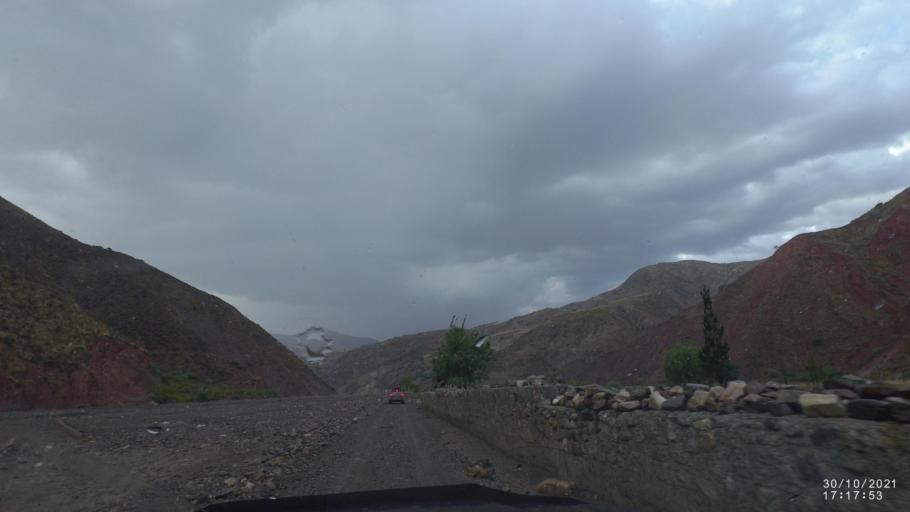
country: BO
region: Cochabamba
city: Colchani
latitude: -17.5374
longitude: -66.6242
